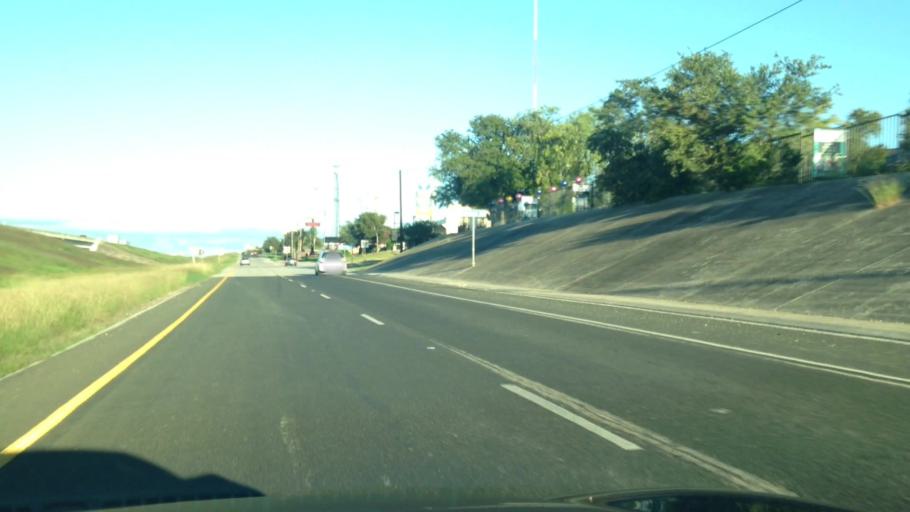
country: US
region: Texas
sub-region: Bexar County
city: Live Oak
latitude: 29.6019
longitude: -98.3896
